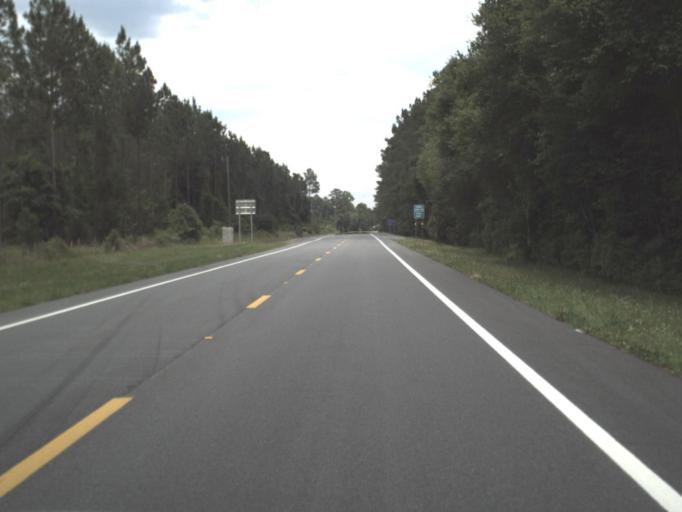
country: US
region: Florida
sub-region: Hamilton County
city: Jasper
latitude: 30.5964
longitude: -82.6720
